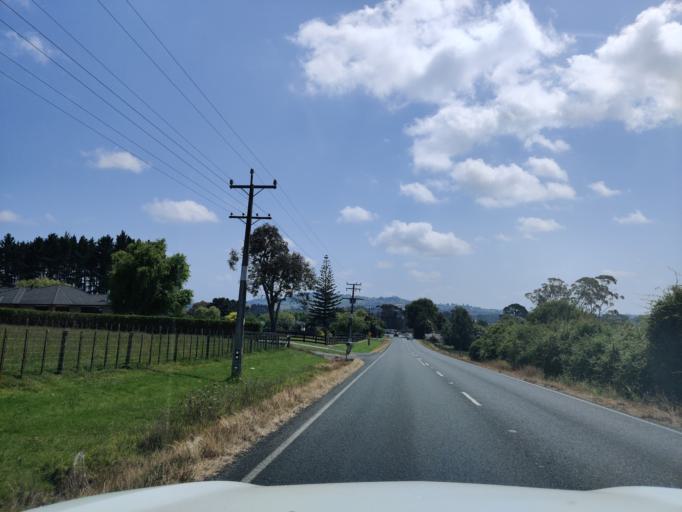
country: NZ
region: Auckland
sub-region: Auckland
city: Pukekohe East
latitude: -37.2142
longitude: 174.9391
